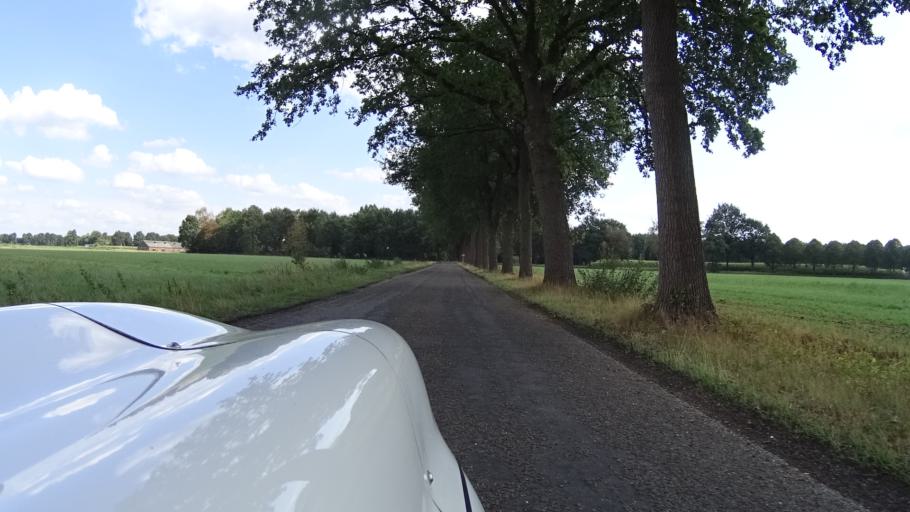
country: NL
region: North Brabant
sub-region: Gemeente Sint Anthonis
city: Sint Anthonis
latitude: 51.6357
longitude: 5.8489
